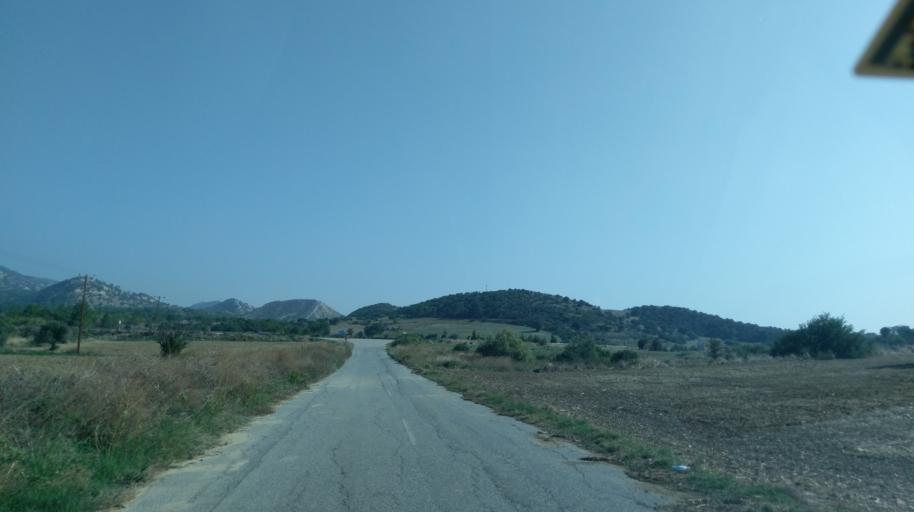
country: CY
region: Ammochostos
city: Lefkonoiko
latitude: 35.3314
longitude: 33.7183
